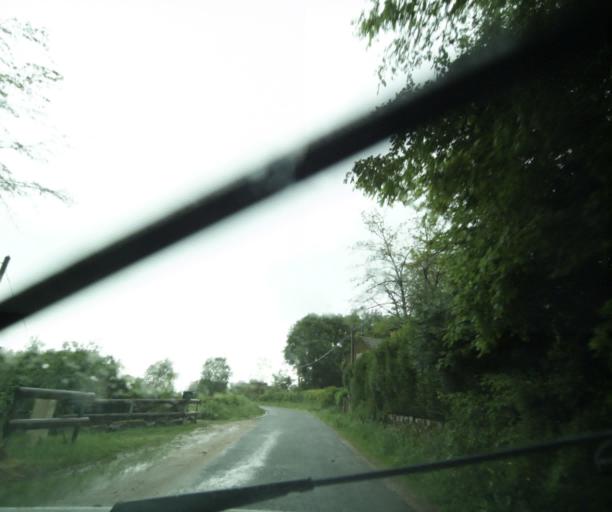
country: FR
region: Bourgogne
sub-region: Departement de Saone-et-Loire
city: Ciry-le-Noble
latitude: 46.5287
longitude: 4.3038
